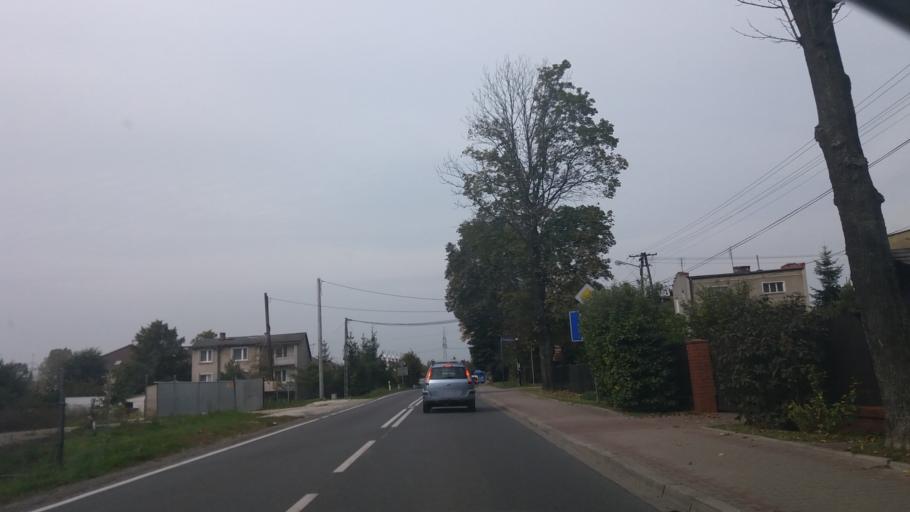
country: PL
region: Lesser Poland Voivodeship
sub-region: Powiat chrzanowski
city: Pogorzyce
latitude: 50.1253
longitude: 19.4323
